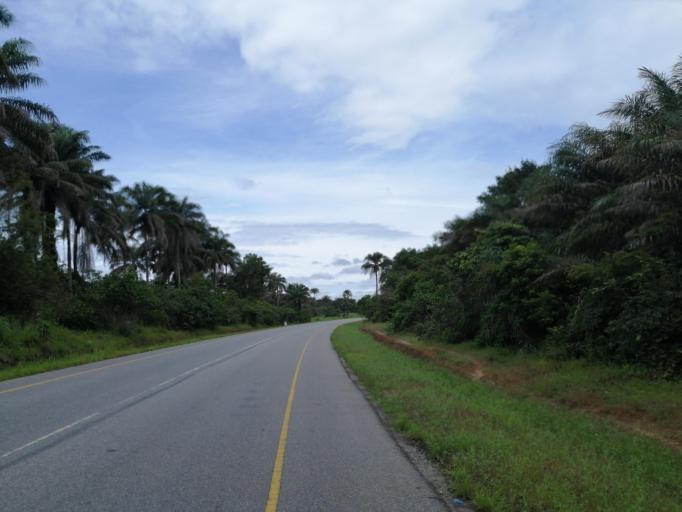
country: SL
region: Northern Province
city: Port Loko
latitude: 8.7579
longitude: -12.9114
